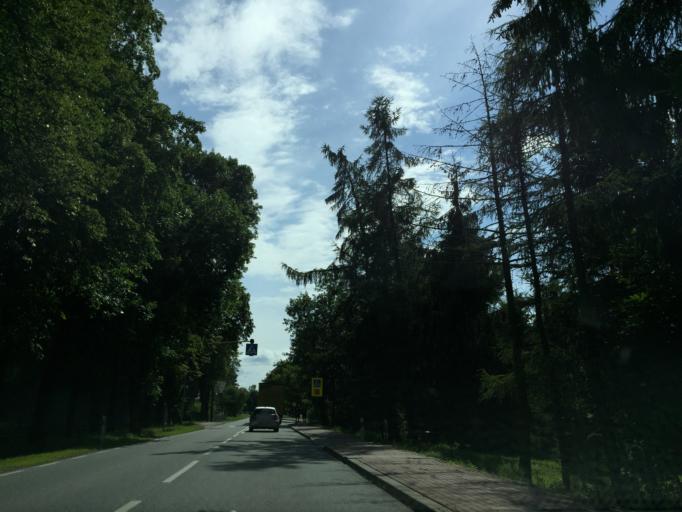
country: PL
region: Masovian Voivodeship
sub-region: Powiat losicki
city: Sarnaki
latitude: 52.2996
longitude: 22.8259
